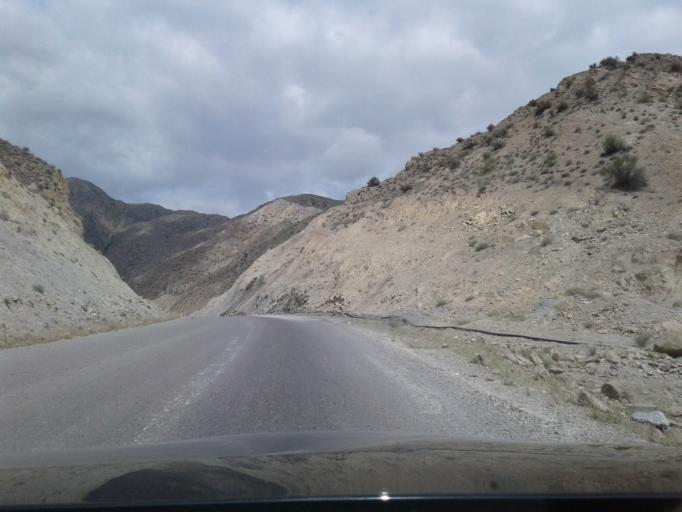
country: TM
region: Ahal
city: Baharly
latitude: 38.5065
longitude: 57.0600
